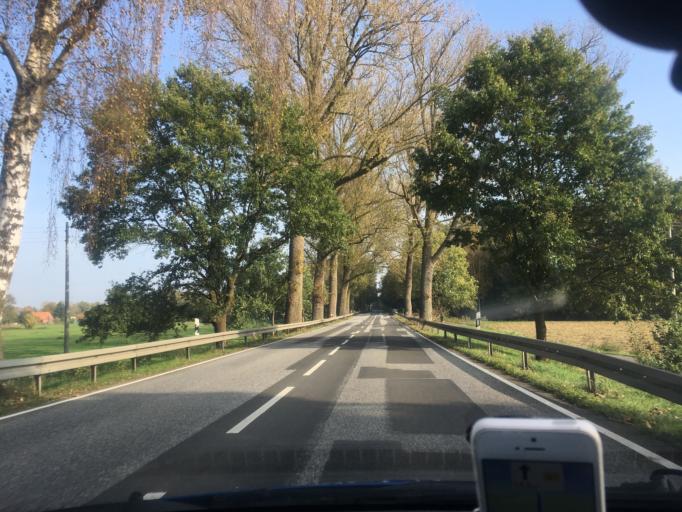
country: DE
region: Mecklenburg-Vorpommern
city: Hagenow
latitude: 53.4632
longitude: 11.2275
